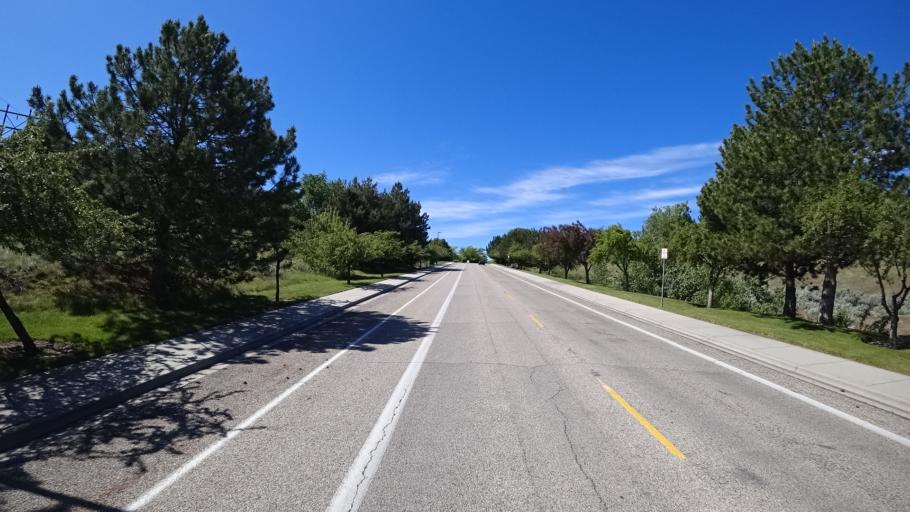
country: US
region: Idaho
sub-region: Ada County
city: Boise
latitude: 43.5455
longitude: -116.1541
